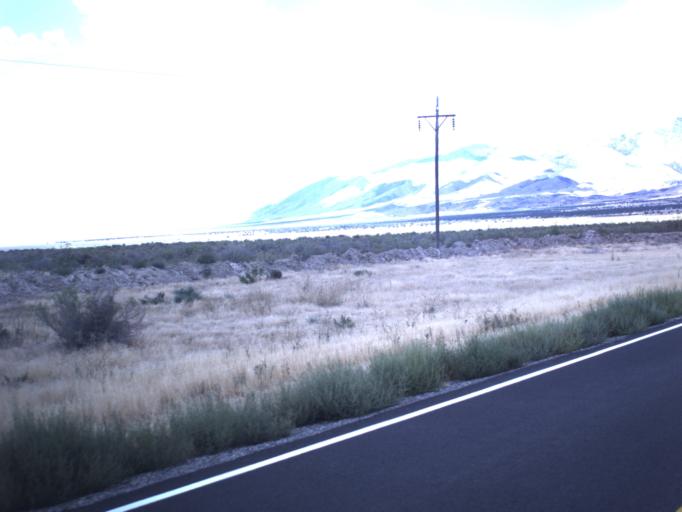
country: US
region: Utah
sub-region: Tooele County
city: Grantsville
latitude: 40.2808
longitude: -112.6703
